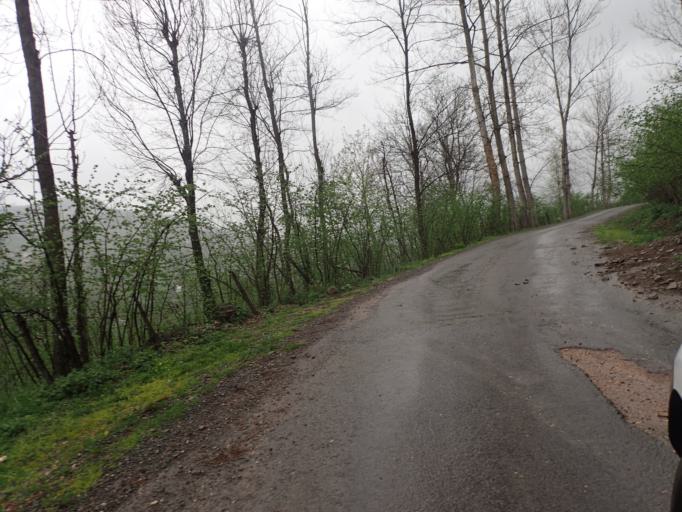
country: TR
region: Ordu
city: Korgan
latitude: 40.7847
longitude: 37.3433
